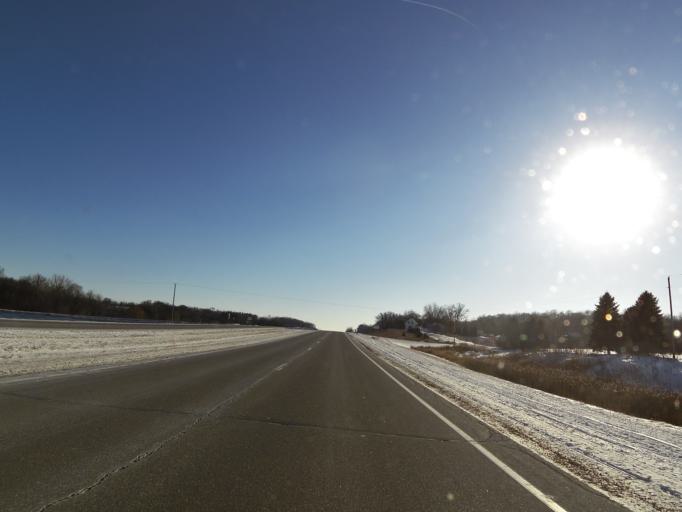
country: US
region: Minnesota
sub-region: Le Sueur County
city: New Prague
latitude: 44.5596
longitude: -93.5018
